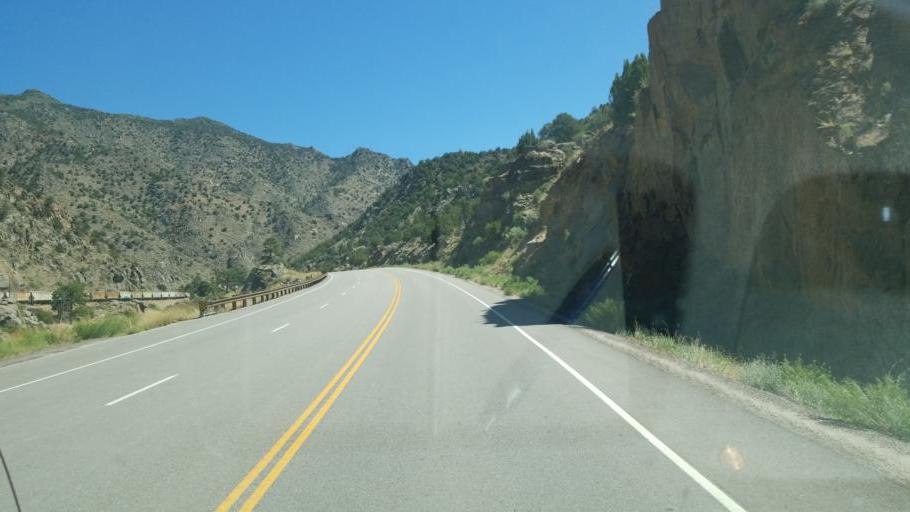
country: US
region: Colorado
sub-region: Fremont County
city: Canon City
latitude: 38.4634
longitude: -105.4534
